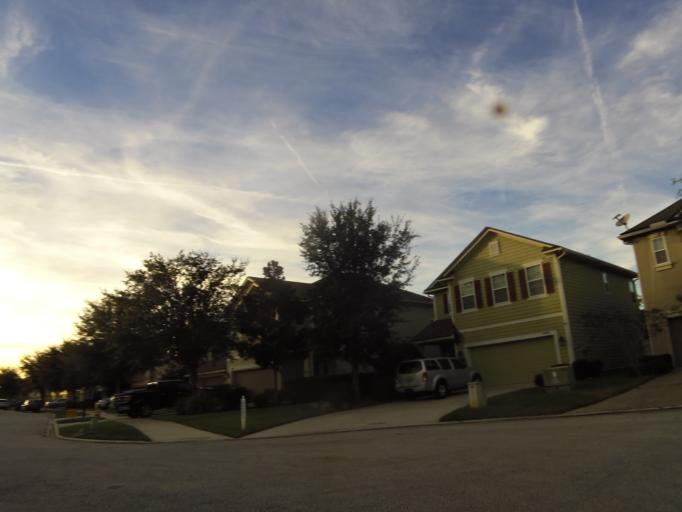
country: US
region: Florida
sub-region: Saint Johns County
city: Fruit Cove
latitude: 30.1612
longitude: -81.5486
